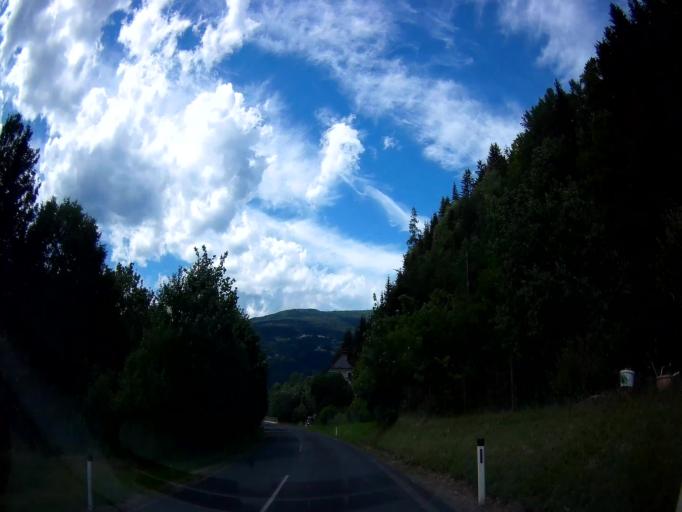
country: AT
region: Styria
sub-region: Politischer Bezirk Murau
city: Stadl an der Mur
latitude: 47.0724
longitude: 13.9847
